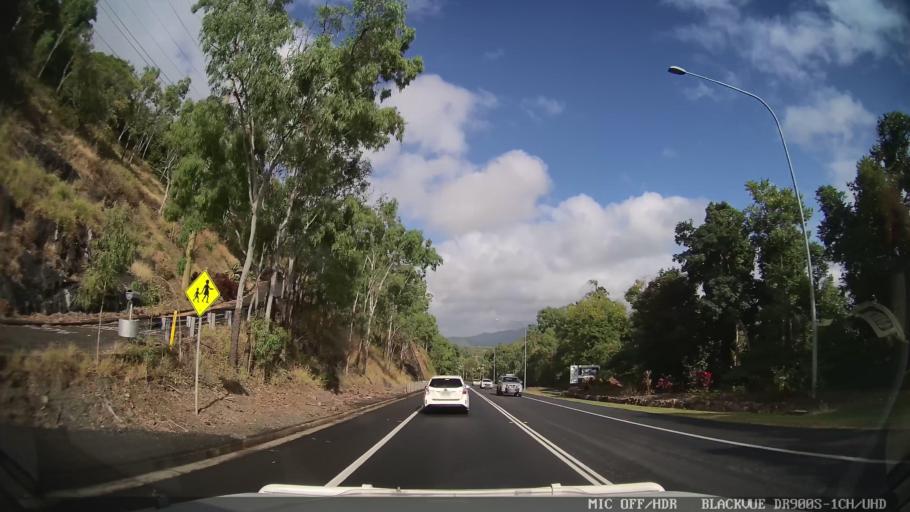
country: AU
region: Queensland
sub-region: Whitsunday
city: Proserpine
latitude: -20.2713
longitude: 148.7085
